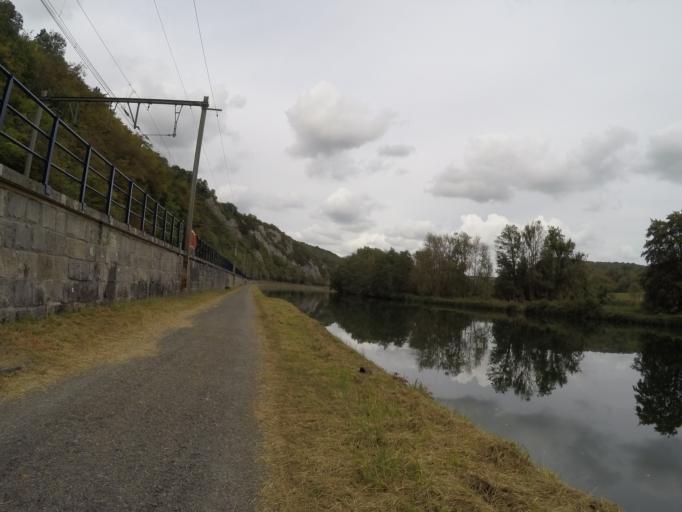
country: BE
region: Wallonia
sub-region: Province de Namur
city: Anhee
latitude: 50.2841
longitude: 4.8914
